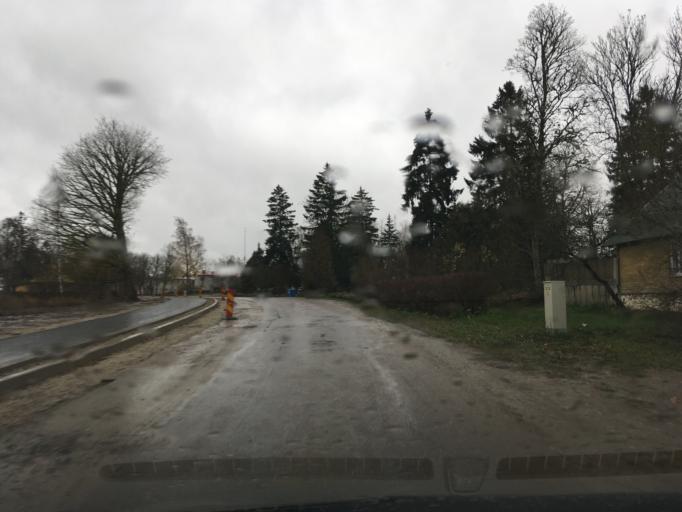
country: EE
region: Laeaene
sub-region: Lihula vald
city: Lihula
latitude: 58.6802
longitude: 23.8234
